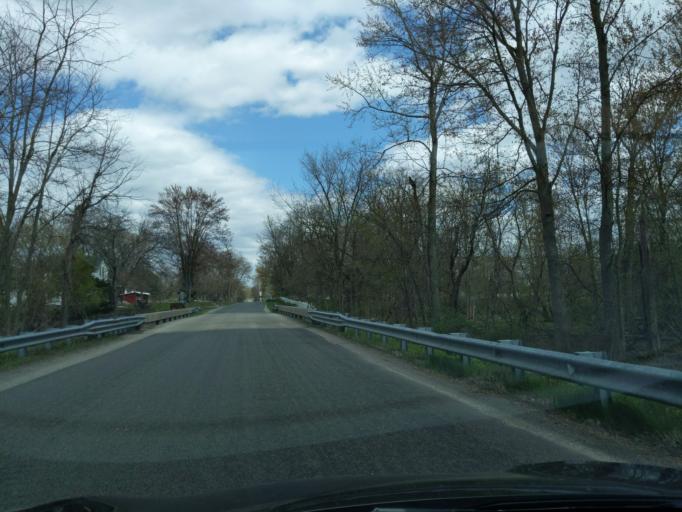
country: US
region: Michigan
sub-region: Ingham County
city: Mason
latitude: 42.6112
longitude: -84.4670
